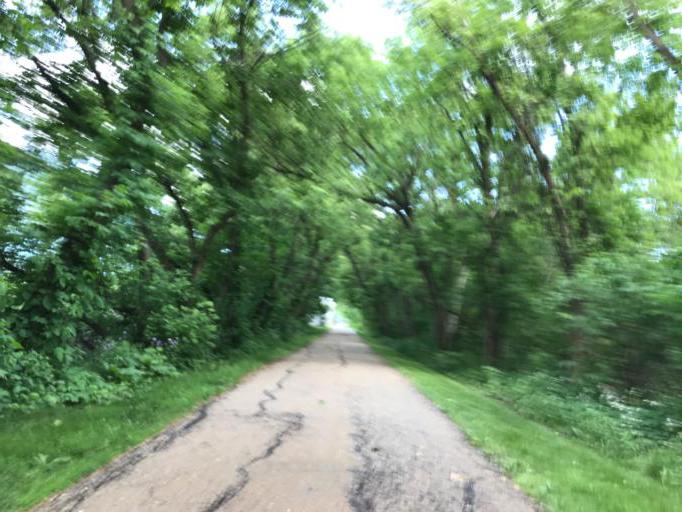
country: US
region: Michigan
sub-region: Oakland County
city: South Lyon
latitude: 42.4561
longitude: -83.6598
